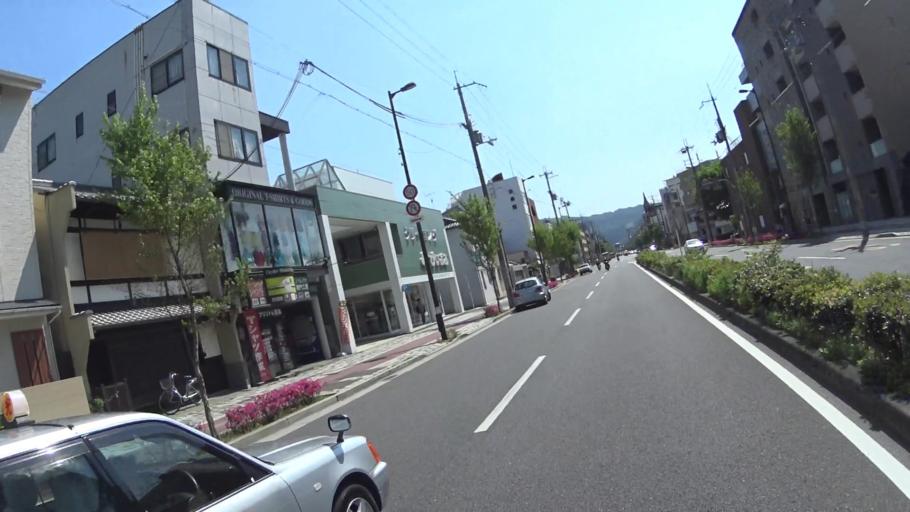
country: JP
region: Kyoto
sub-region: Kyoto-shi
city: Kamigyo-ku
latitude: 35.0443
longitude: 135.7651
